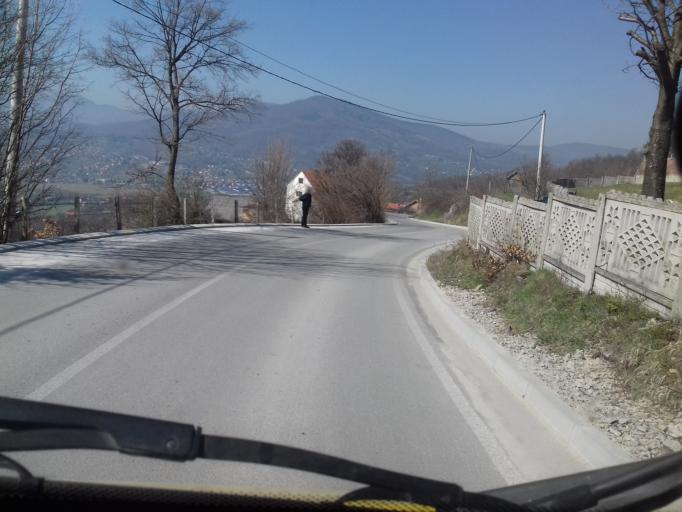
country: BA
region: Federation of Bosnia and Herzegovina
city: Travnik
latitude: 44.2253
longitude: 17.7145
